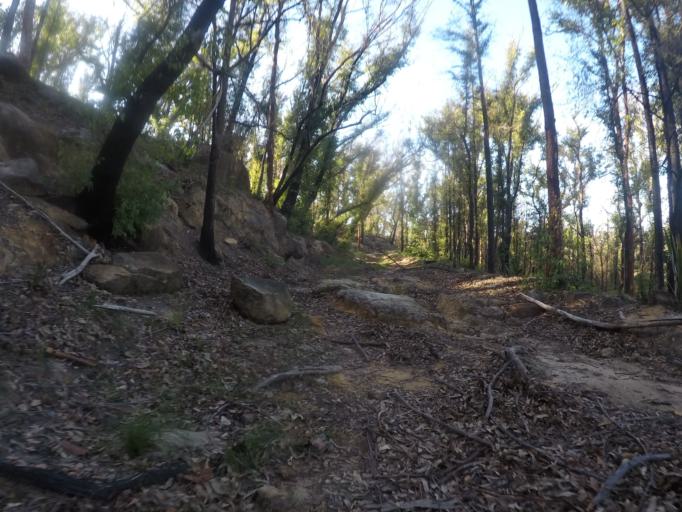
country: AU
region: New South Wales
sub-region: Hornsby Shire
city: Glenorie
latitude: -33.3433
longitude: 151.0479
